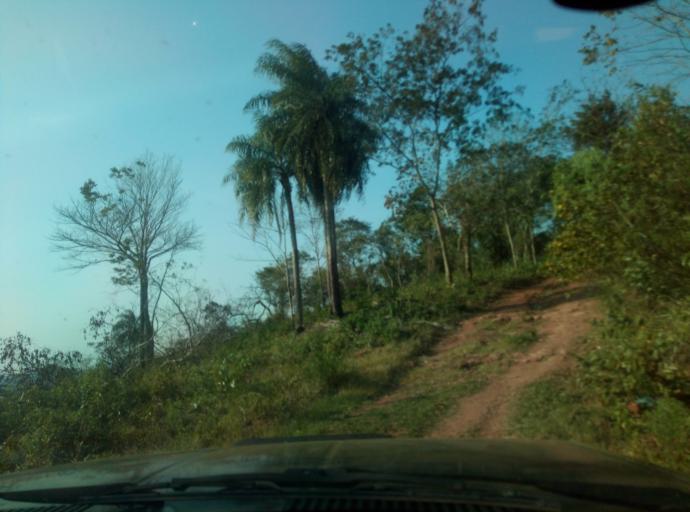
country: PY
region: Caaguazu
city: San Joaquin
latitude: -25.1560
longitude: -56.1213
